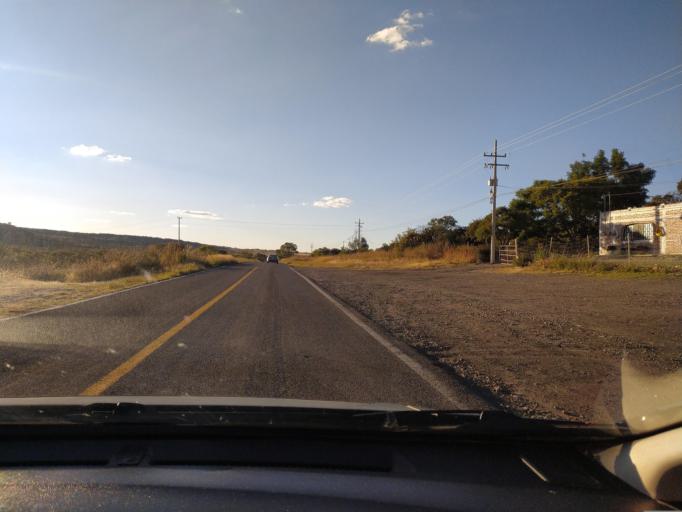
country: MX
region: Jalisco
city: San Julian
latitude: 21.0034
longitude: -102.1090
